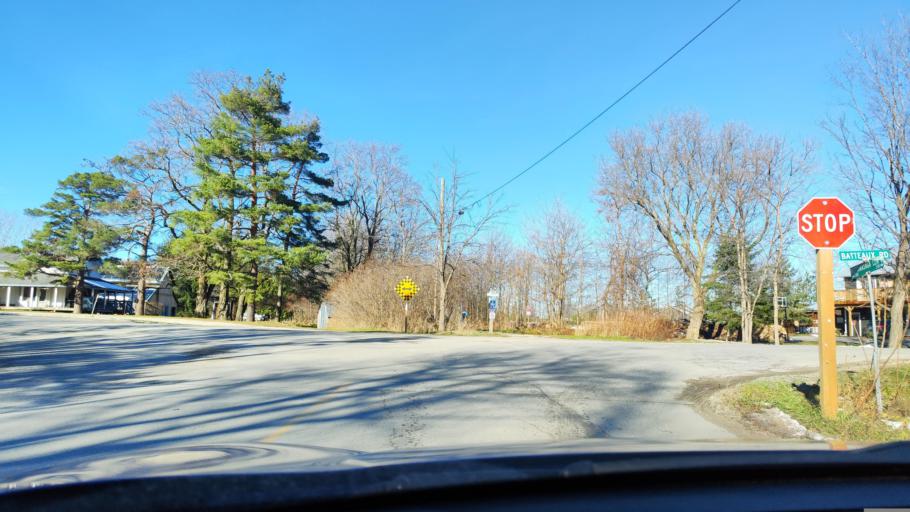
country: CA
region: Ontario
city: Collingwood
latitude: 44.4661
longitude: -80.1746
